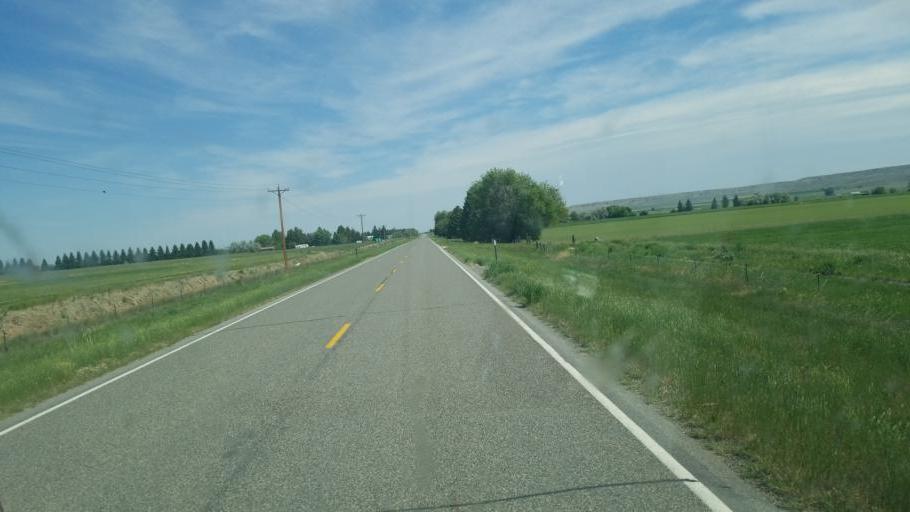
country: US
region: Wyoming
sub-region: Park County
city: Powell
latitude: 44.7328
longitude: -108.9327
